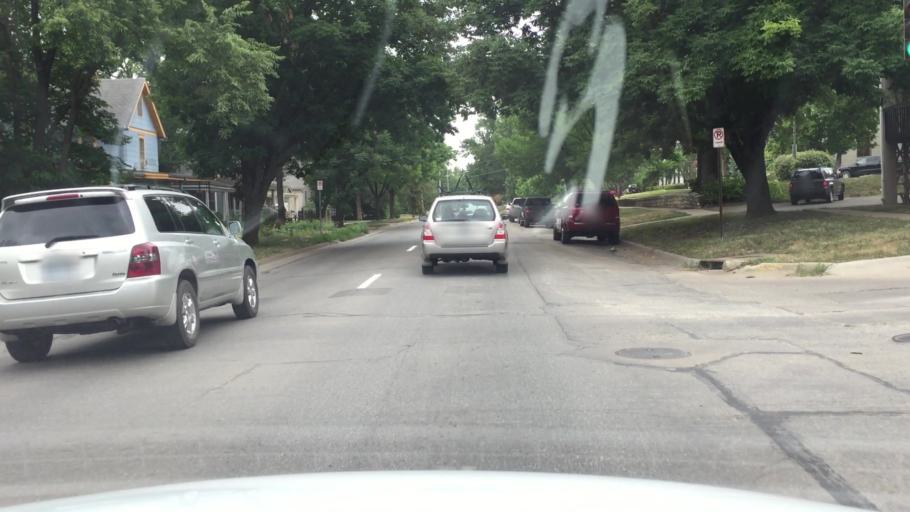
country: US
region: Kansas
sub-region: Douglas County
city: Lawrence
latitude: 38.9582
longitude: -95.2394
